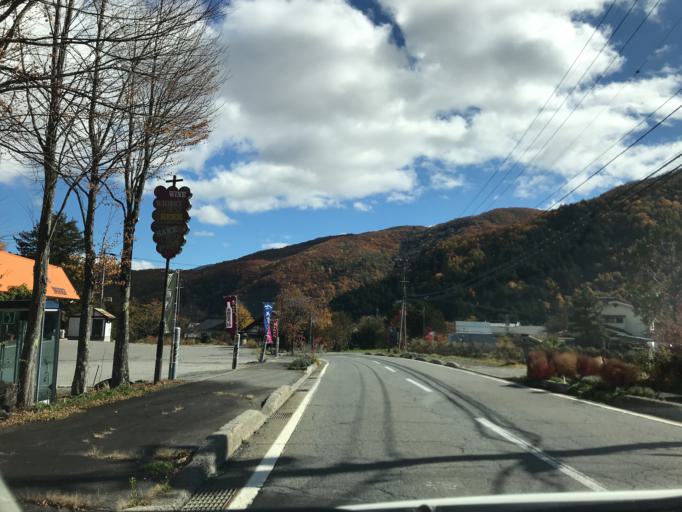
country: JP
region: Nagano
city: Toyoshina
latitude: 36.1244
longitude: 137.6525
